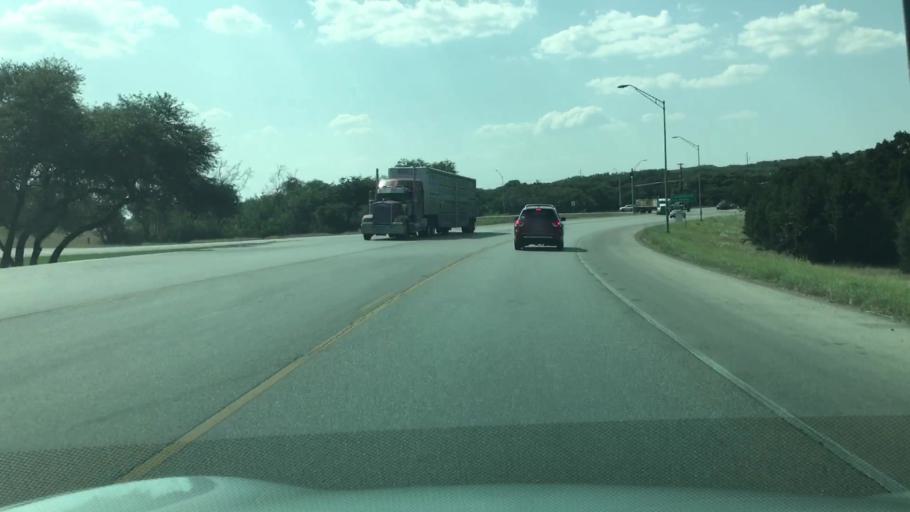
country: US
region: Texas
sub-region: Hays County
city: Wimberley
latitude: 29.9413
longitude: -98.0904
